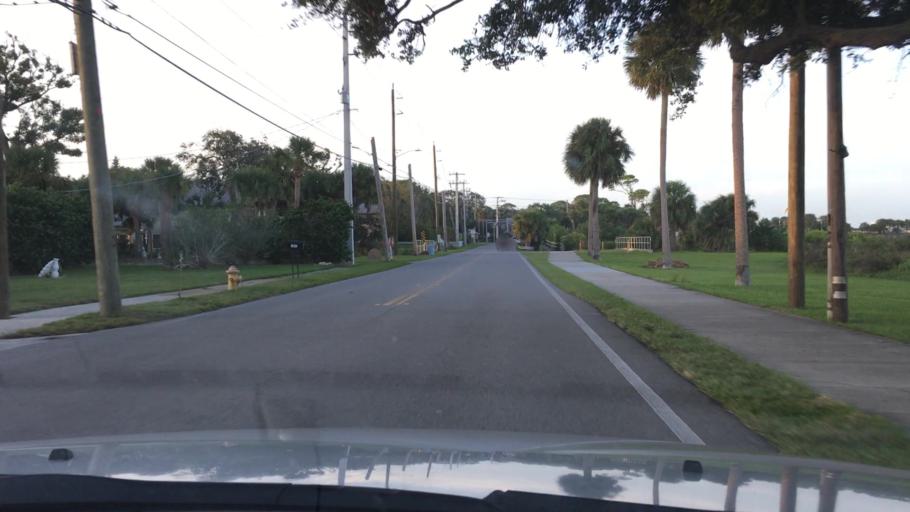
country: US
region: Florida
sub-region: Volusia County
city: Holly Hill
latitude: 29.2453
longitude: -81.0363
